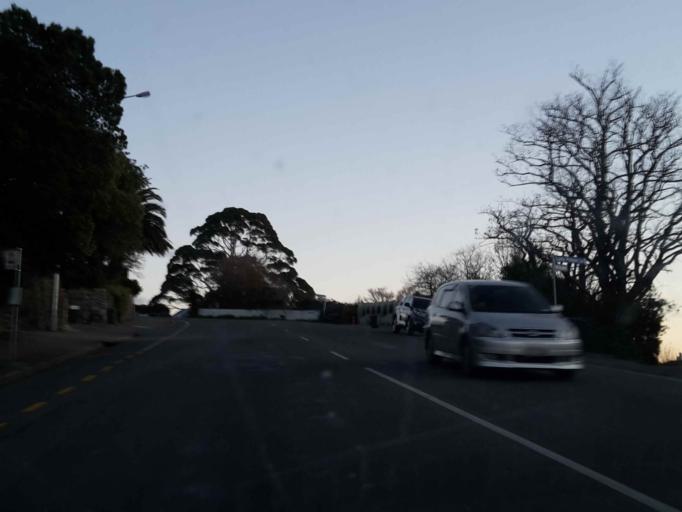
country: NZ
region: Canterbury
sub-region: Christchurch City
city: Christchurch
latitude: -43.5757
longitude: 172.6246
